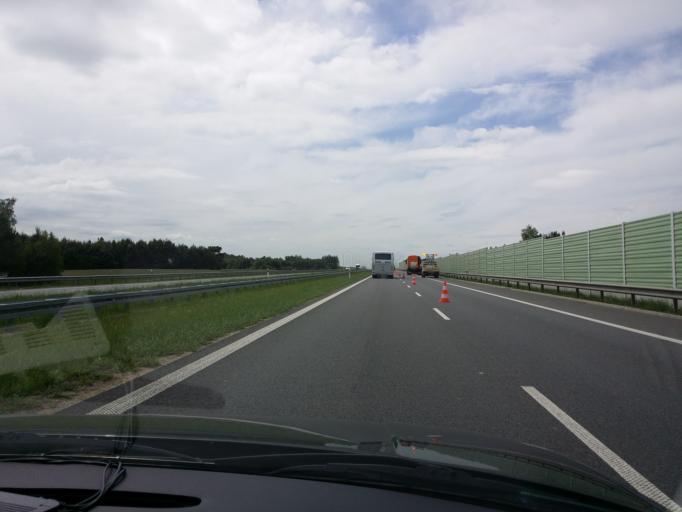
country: PL
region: Masovian Voivodeship
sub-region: Powiat szydlowiecki
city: Oronsko
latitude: 51.3064
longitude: 21.0038
